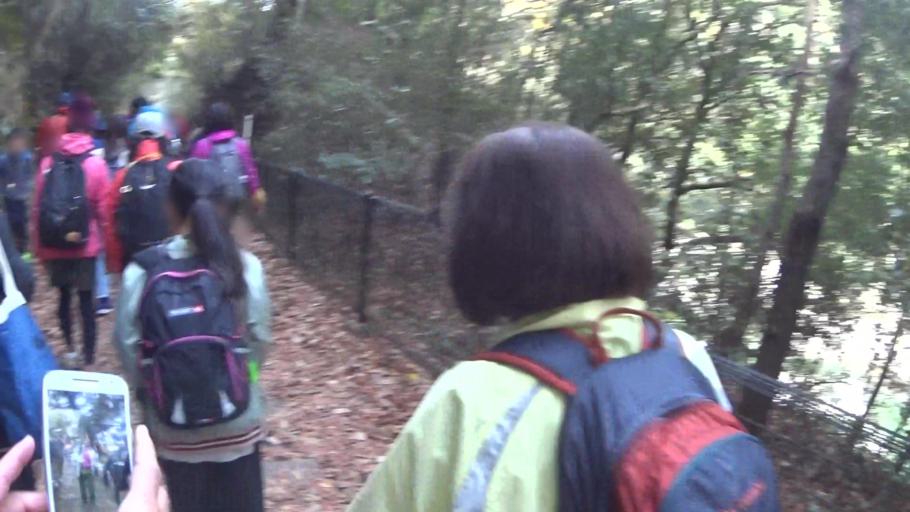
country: JP
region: Hyogo
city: Takarazuka
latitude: 34.8447
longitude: 135.3171
